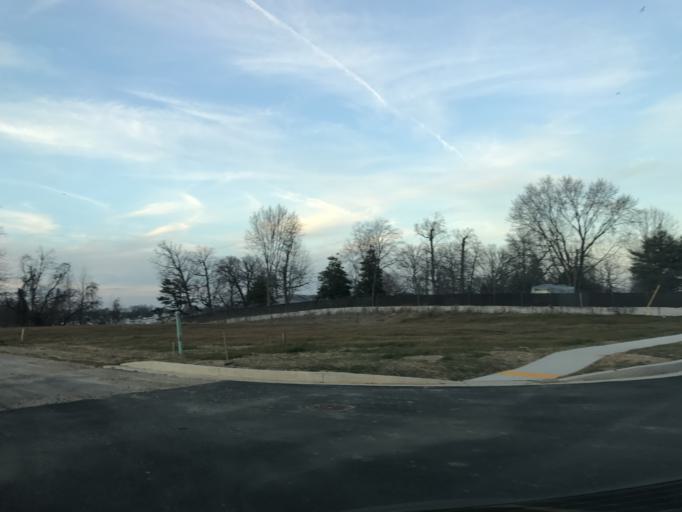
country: US
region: Maryland
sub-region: Baltimore County
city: Middle River
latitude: 39.3020
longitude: -76.4187
